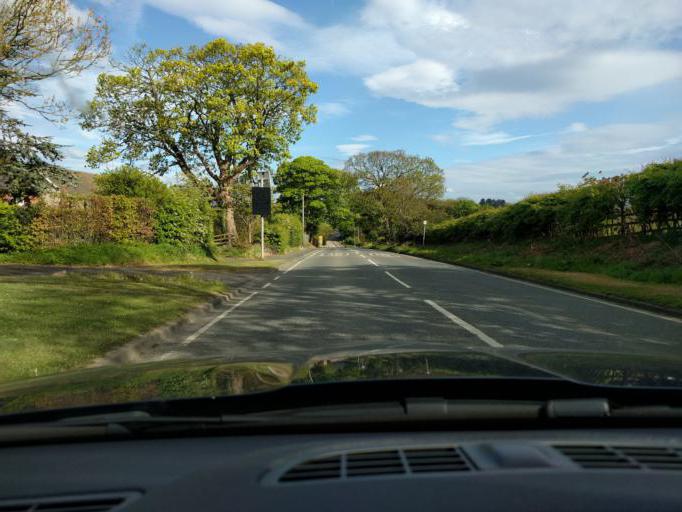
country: GB
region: England
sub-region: Northumberland
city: Morpeth
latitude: 55.1510
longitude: -1.6632
